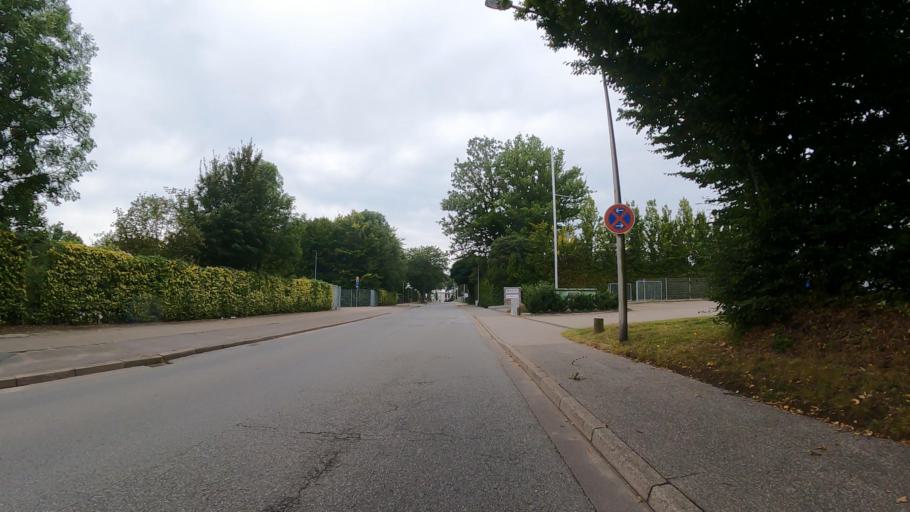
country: DE
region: Schleswig-Holstein
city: Pinneberg
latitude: 53.6647
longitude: 9.7819
